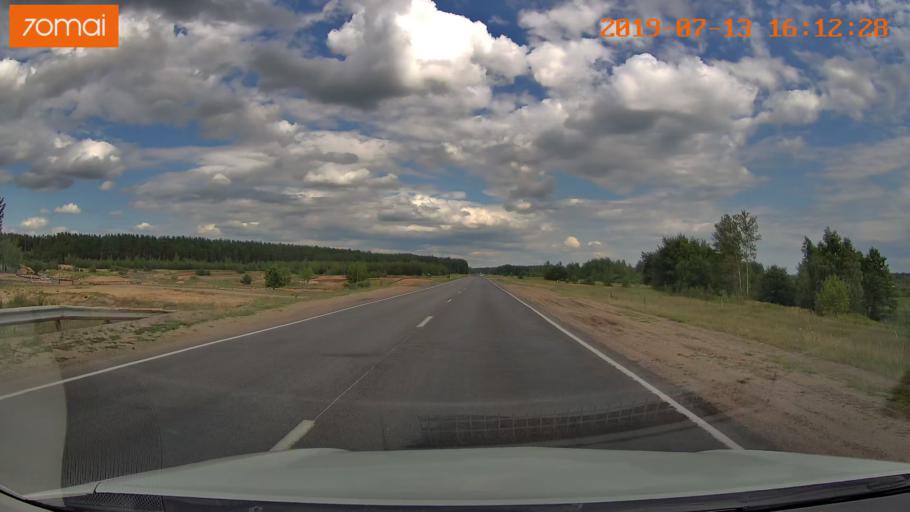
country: BY
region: Mogilev
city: Babruysk
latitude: 53.1669
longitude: 29.2809
